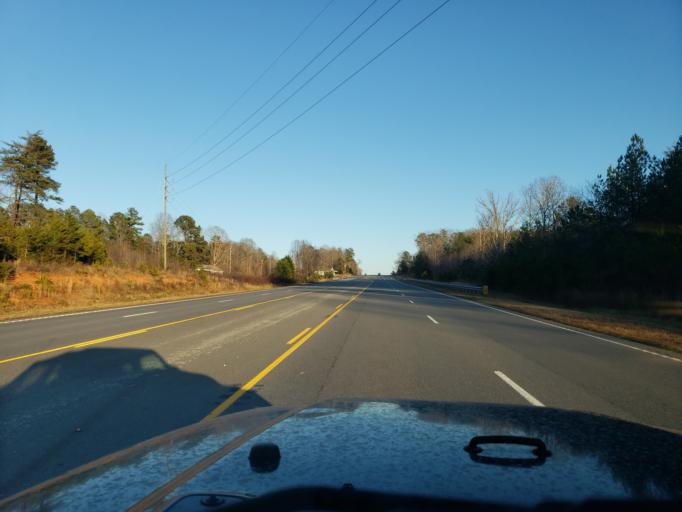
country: US
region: South Carolina
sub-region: Cherokee County
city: Blacksburg
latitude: 35.0763
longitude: -81.4283
